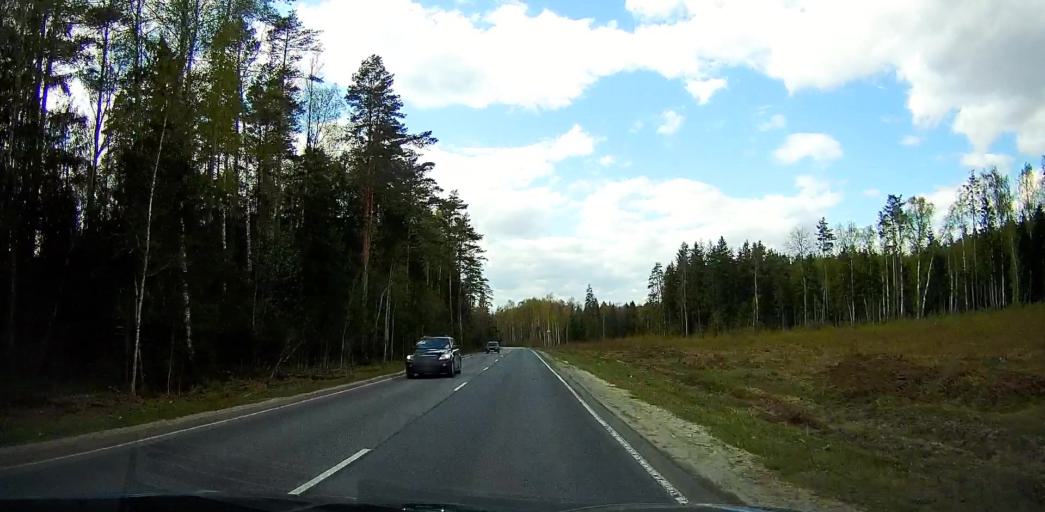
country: RU
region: Moskovskaya
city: Rakhmanovo
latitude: 55.6506
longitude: 38.6607
